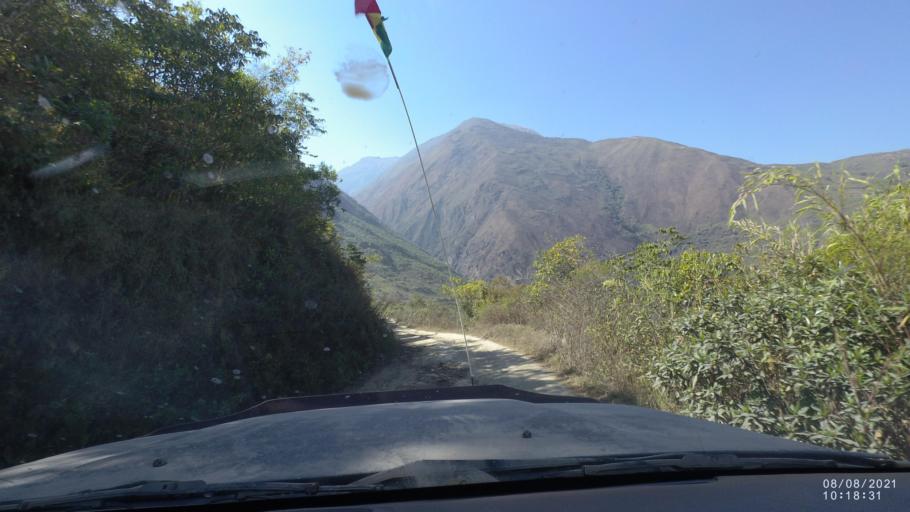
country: BO
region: La Paz
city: Quime
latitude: -16.6857
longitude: -66.7306
